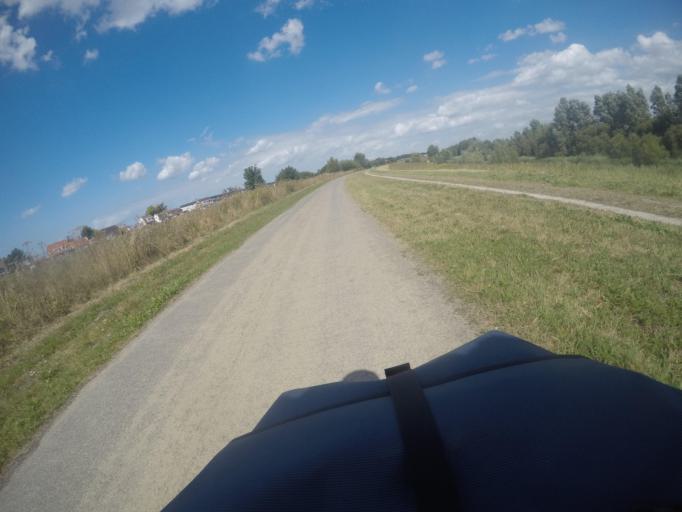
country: NL
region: North Holland
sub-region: Gemeente Haarlemmermeer
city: Hoofddorp
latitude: 52.3578
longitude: 4.7562
